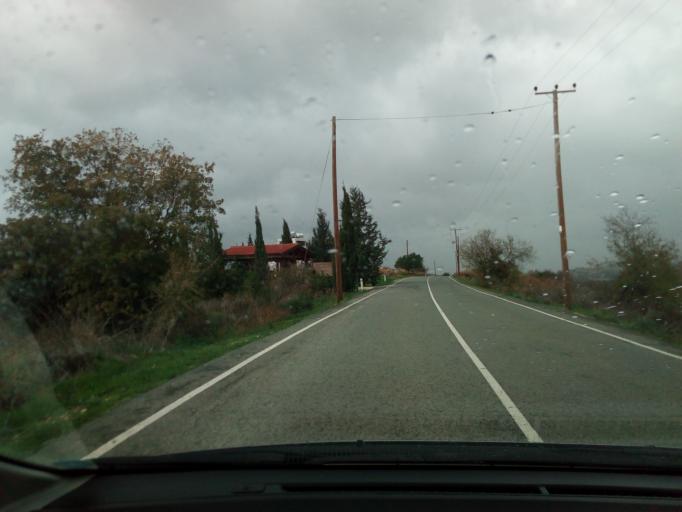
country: CY
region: Pafos
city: Polis
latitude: 34.9542
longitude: 32.4827
